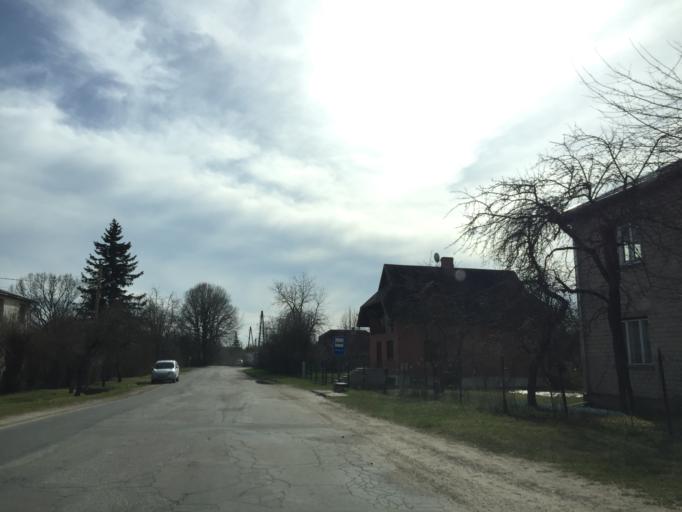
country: LV
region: Ogre
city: Ogre
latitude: 56.8192
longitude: 24.5890
